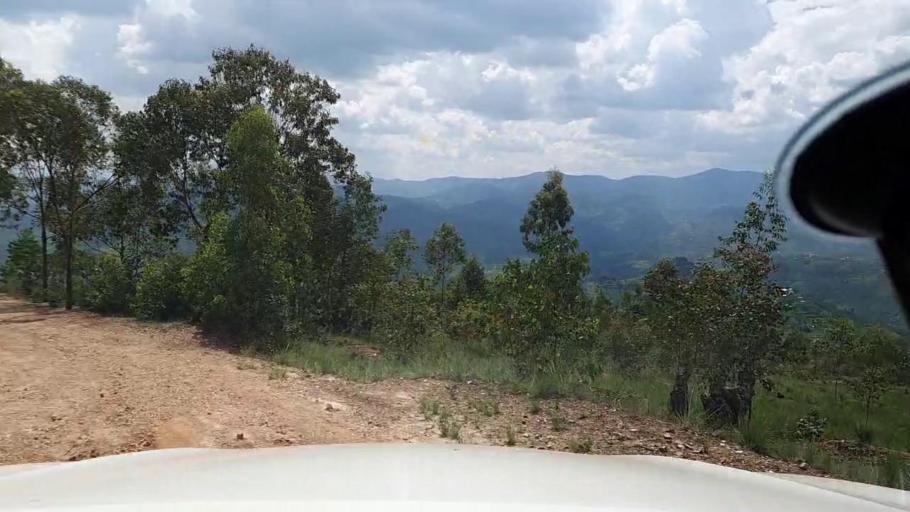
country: RW
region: Southern Province
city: Gitarama
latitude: -1.8404
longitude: 29.8209
